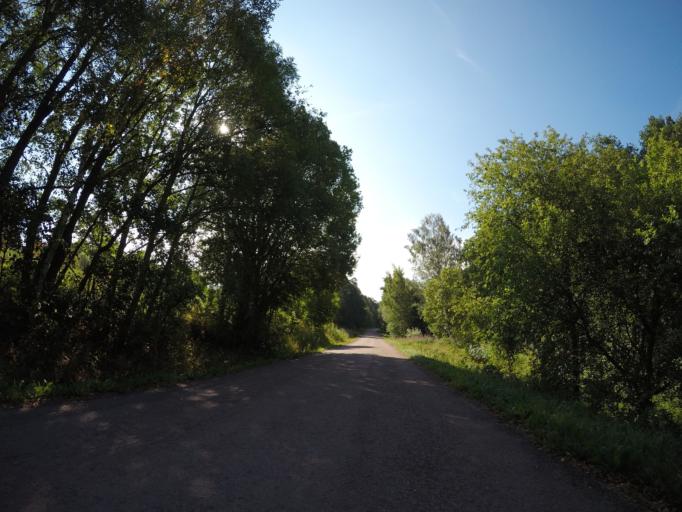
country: AX
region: Alands landsbygd
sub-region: Finstroem
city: Finstroem
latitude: 60.2699
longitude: 19.9262
